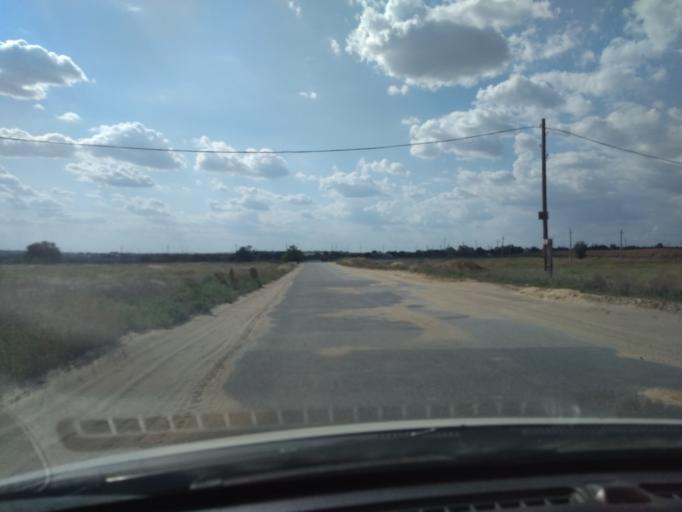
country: RU
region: Volgograd
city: Vodstroy
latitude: 48.8060
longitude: 44.5274
